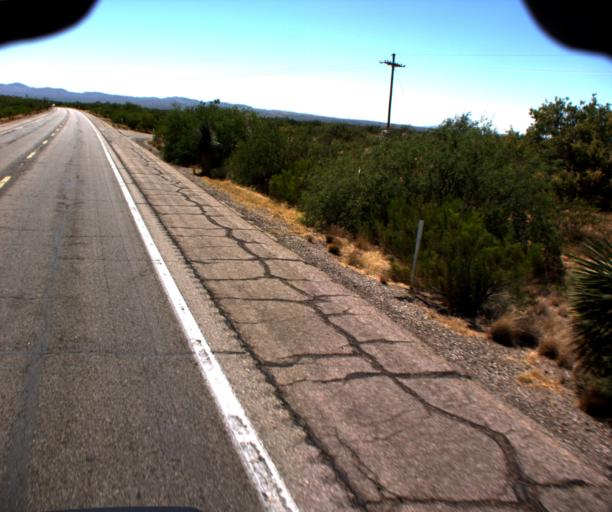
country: US
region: Arizona
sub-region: Pinal County
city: Oracle
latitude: 32.6105
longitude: -110.8464
